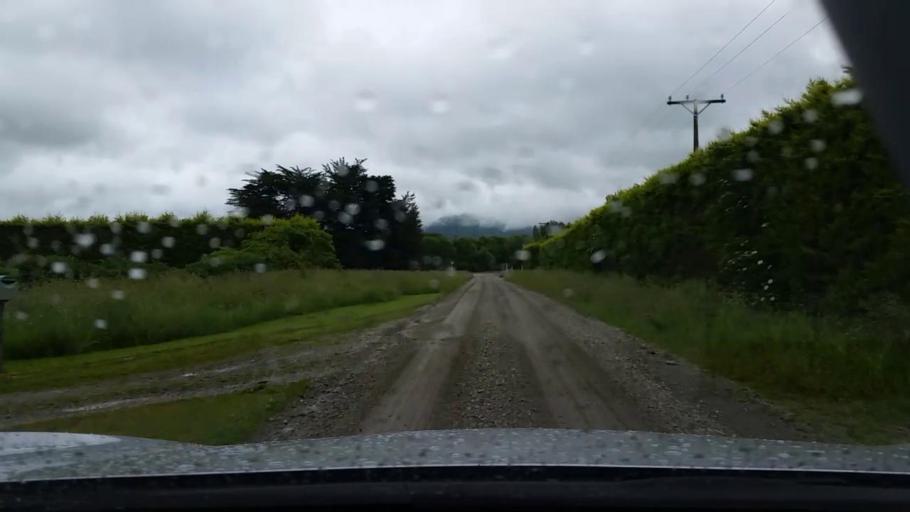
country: NZ
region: Southland
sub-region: Gore District
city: Gore
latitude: -46.0706
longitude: 168.9542
